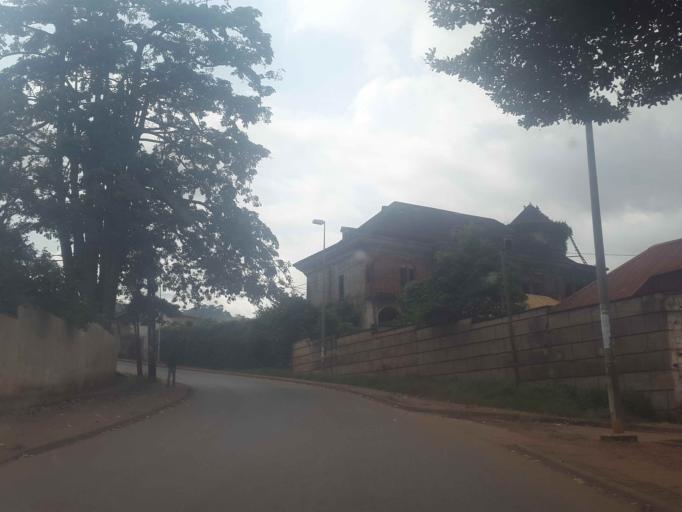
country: CM
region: Centre
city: Yaounde
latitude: 3.8745
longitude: 11.4847
